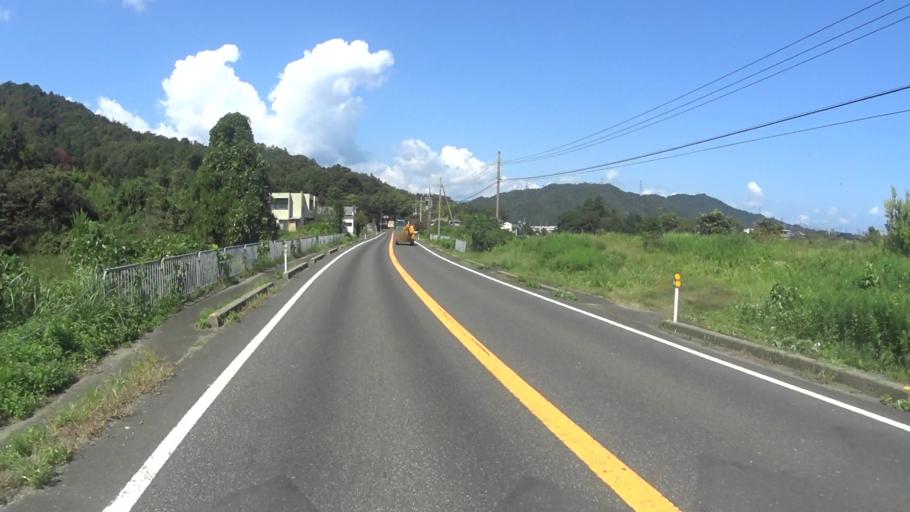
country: JP
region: Kyoto
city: Miyazu
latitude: 35.5418
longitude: 135.2347
